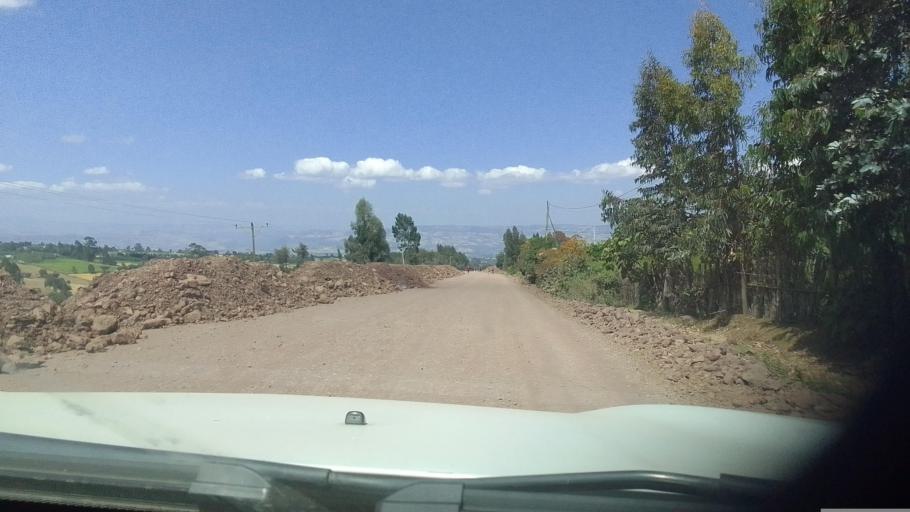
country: ET
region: Oromiya
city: Hagere Hiywet
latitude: 8.8572
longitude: 37.8920
